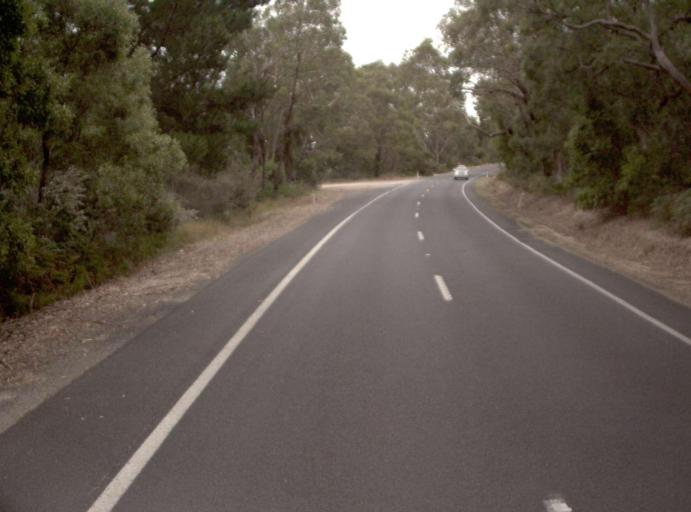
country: AU
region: Victoria
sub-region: Wellington
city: Sale
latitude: -38.2149
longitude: 147.0620
